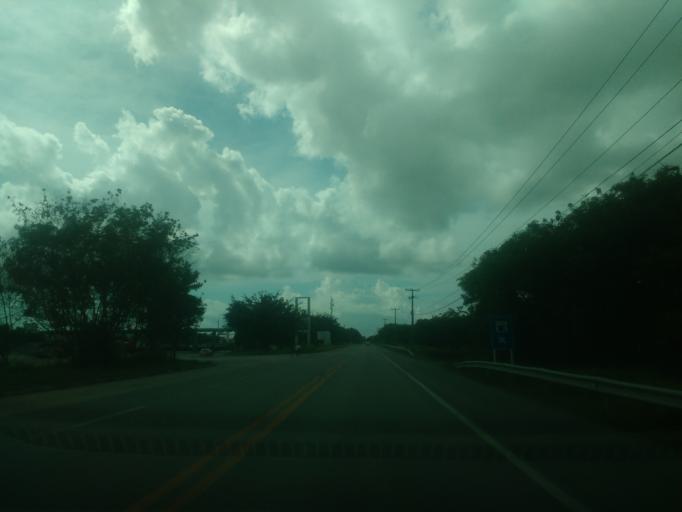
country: BR
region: Alagoas
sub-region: Marechal Deodoro
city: Marechal Deodoro
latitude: -9.6702
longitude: -35.8415
